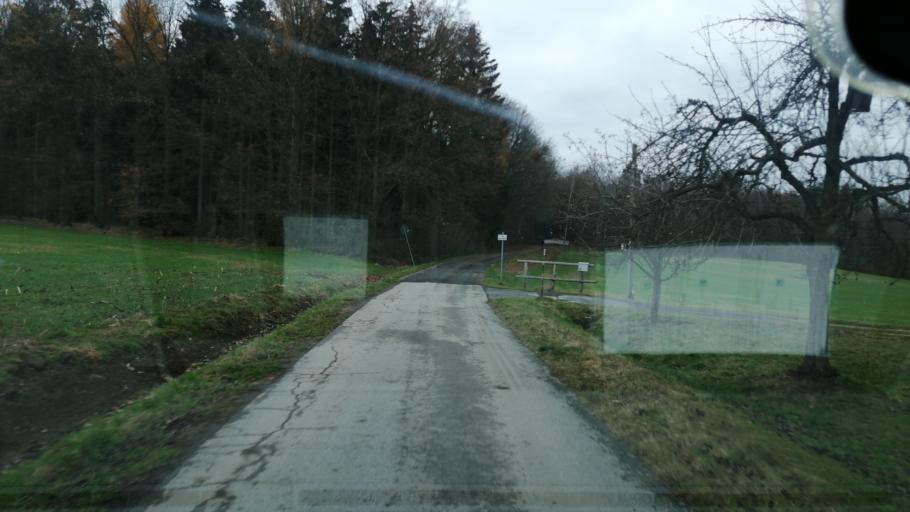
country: DE
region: Saxony
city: Bernstadt
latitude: 51.0553
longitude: 14.7869
